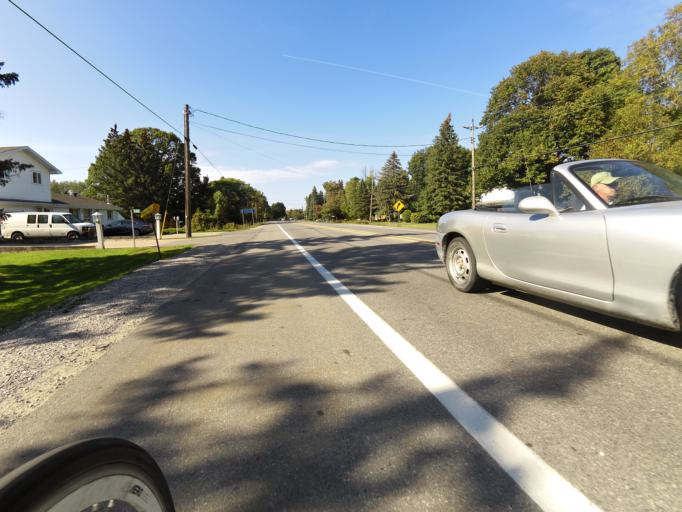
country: CA
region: Ontario
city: Bells Corners
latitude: 45.2530
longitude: -75.6974
